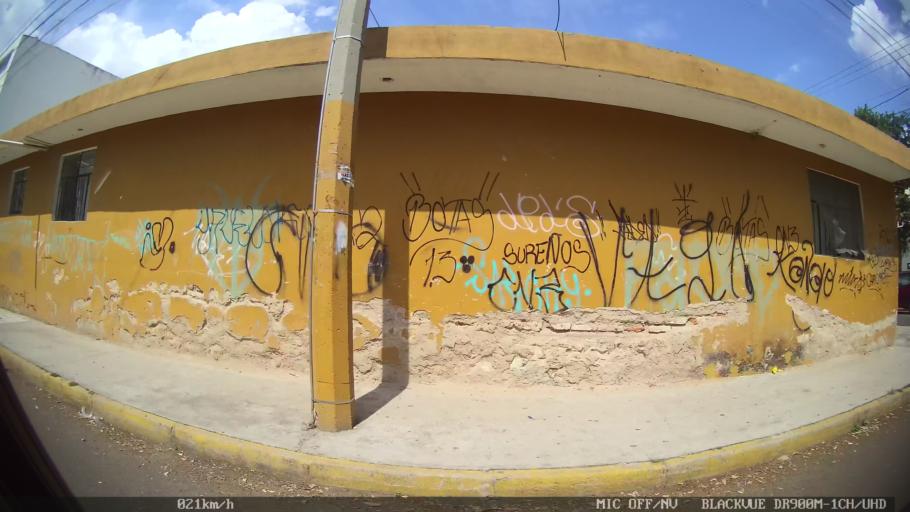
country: MX
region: Jalisco
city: Tonala
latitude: 20.6245
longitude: -103.2635
